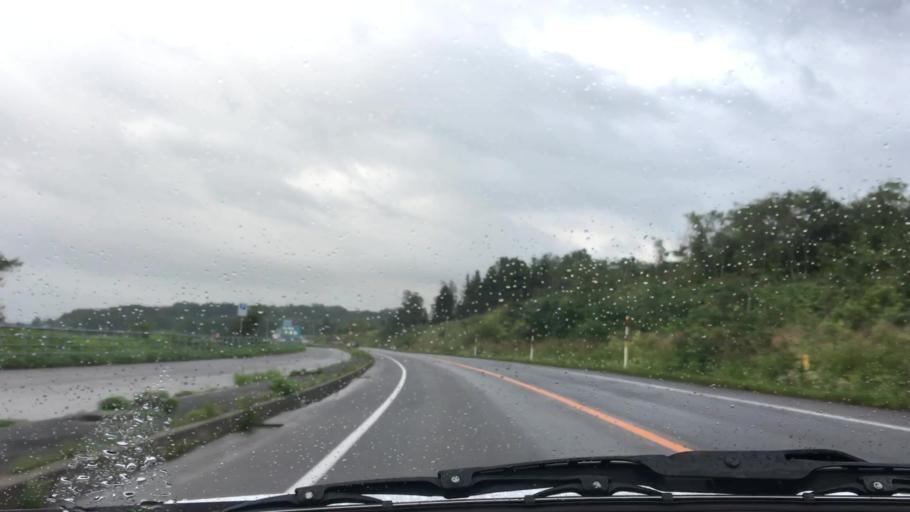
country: JP
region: Hokkaido
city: Nanae
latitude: 42.1811
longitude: 140.4398
